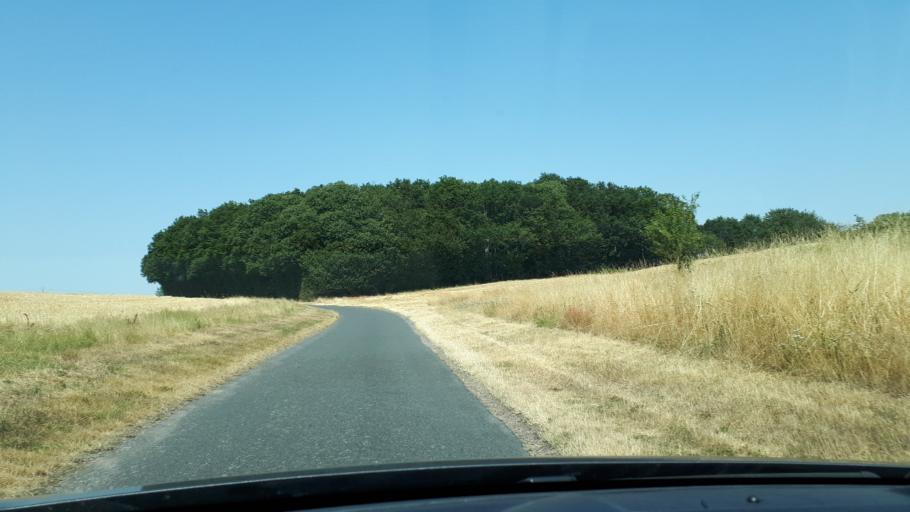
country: FR
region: Centre
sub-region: Departement du Loir-et-Cher
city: Saint-Ouen
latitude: 47.8209
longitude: 1.0645
